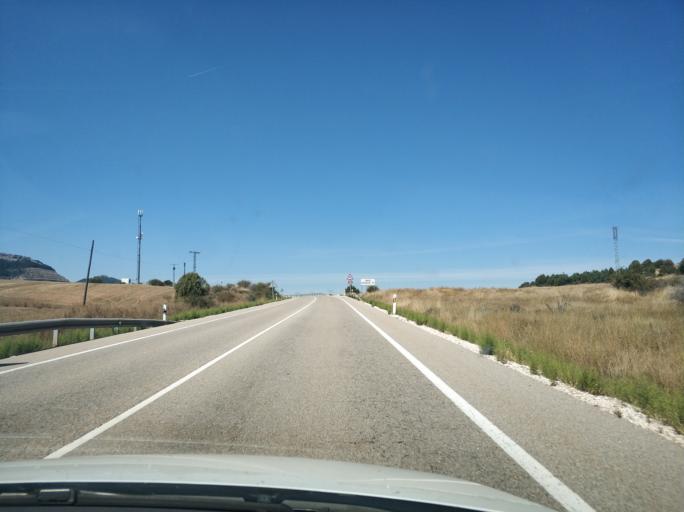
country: ES
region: Castille and Leon
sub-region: Provincia de Burgos
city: Mambrillas de Lara
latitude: 42.0927
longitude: -3.4663
